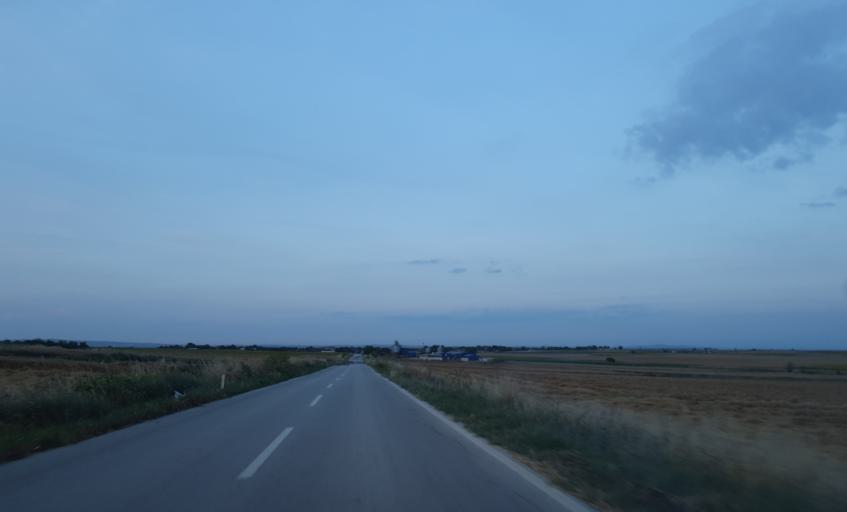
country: TR
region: Tekirdag
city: Beyazkoy
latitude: 41.4287
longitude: 27.6830
